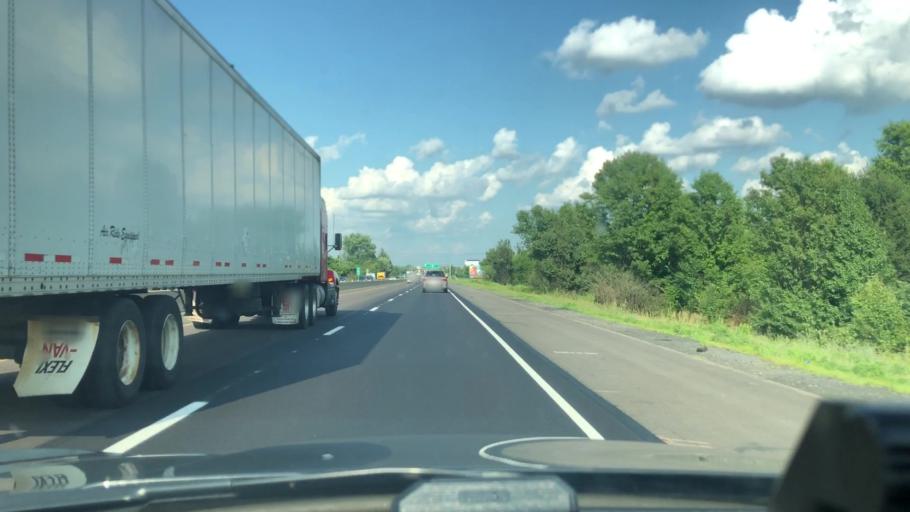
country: US
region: Pennsylvania
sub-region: Lehigh County
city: Breinigsville
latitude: 40.5771
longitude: -75.6367
